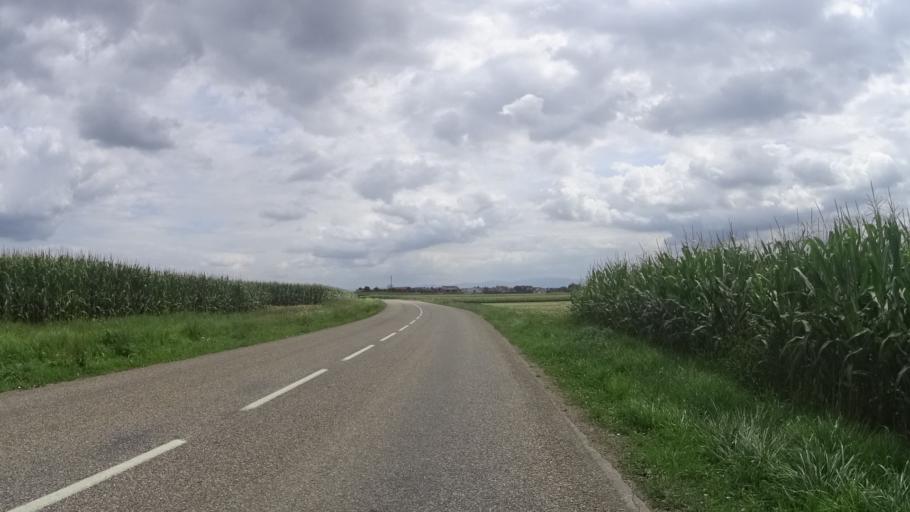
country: FR
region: Alsace
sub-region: Departement du Bas-Rhin
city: Geudertheim
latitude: 48.7213
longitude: 7.7670
